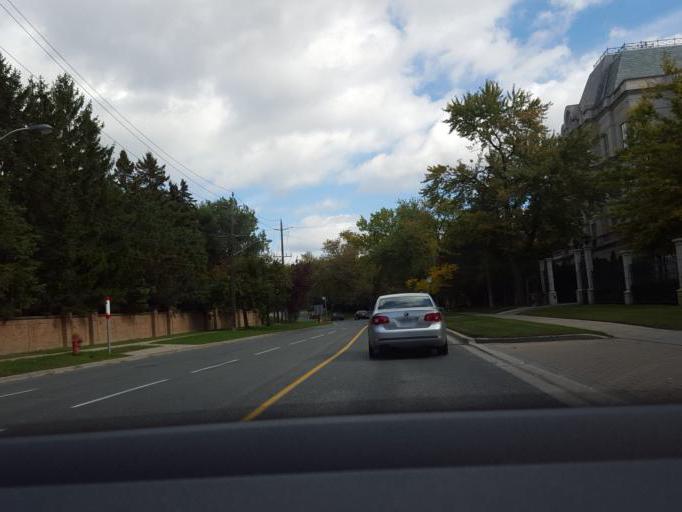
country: CA
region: Ontario
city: Willowdale
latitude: 43.7364
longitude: -79.3809
